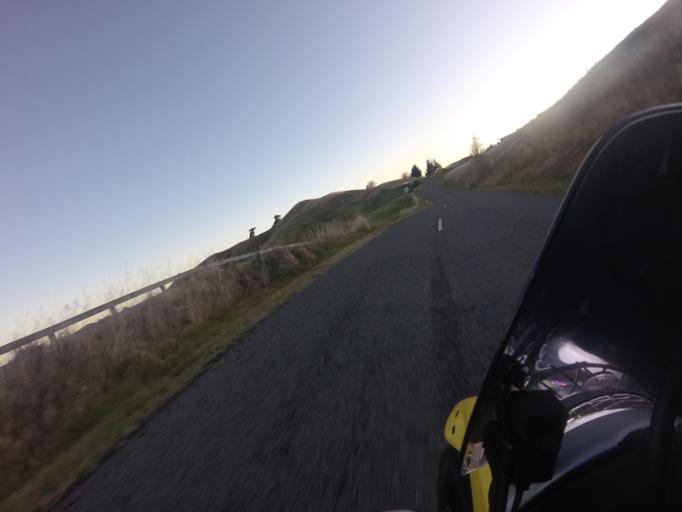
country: NZ
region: Gisborne
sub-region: Gisborne District
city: Gisborne
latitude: -38.6735
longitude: 178.0675
